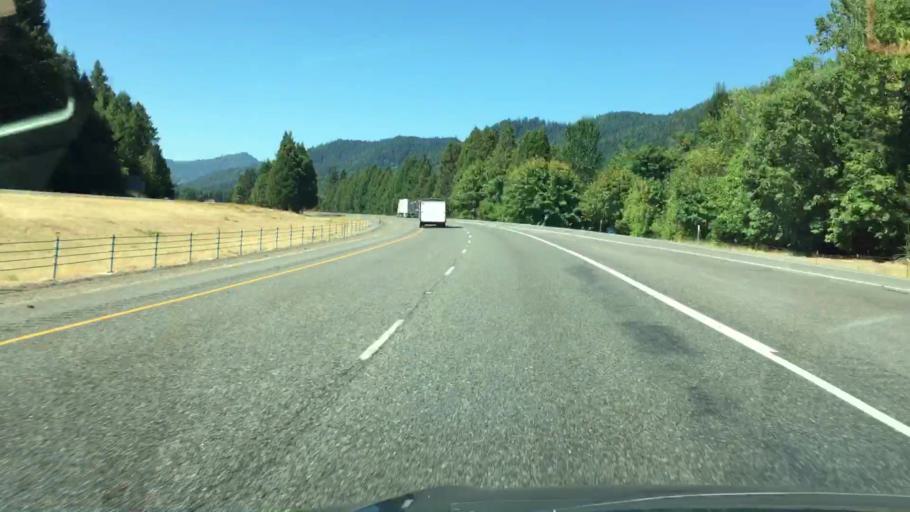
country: US
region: Oregon
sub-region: Douglas County
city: Canyonville
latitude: 42.7674
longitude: -123.3225
